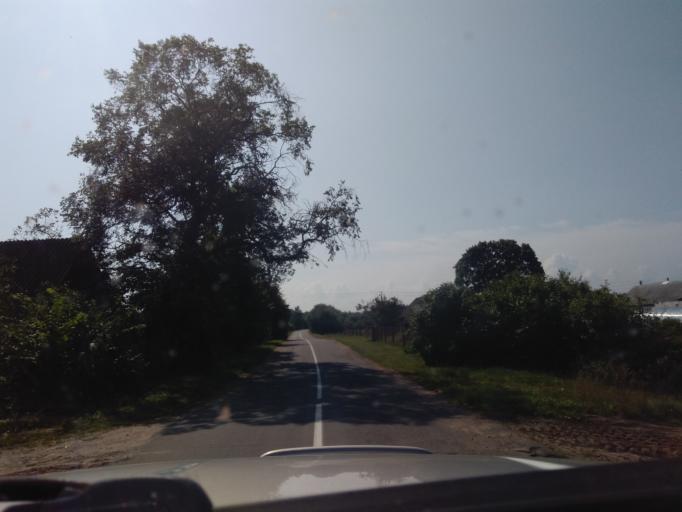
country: BY
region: Minsk
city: Valozhyn
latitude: 54.0172
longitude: 26.6037
